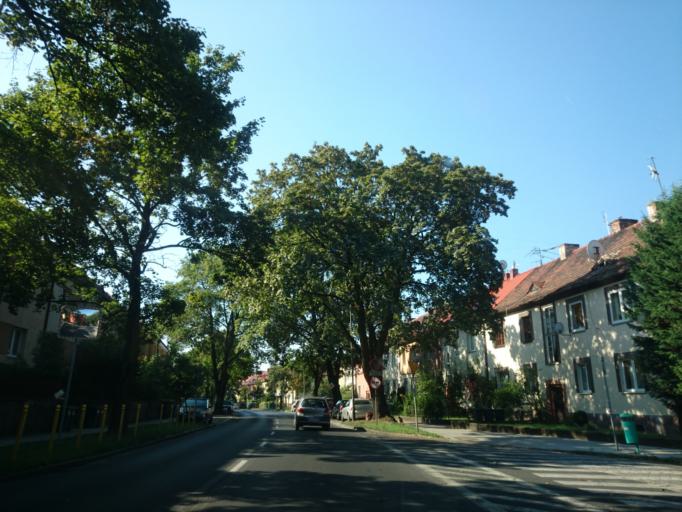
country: PL
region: West Pomeranian Voivodeship
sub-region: Szczecin
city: Szczecin
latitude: 53.4360
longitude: 14.5119
